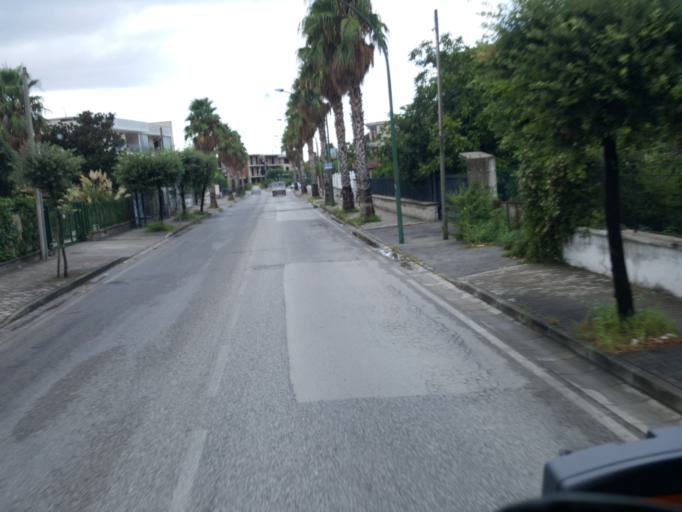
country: IT
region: Campania
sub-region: Provincia di Napoli
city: Palma Campania
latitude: 40.8591
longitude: 14.5504
